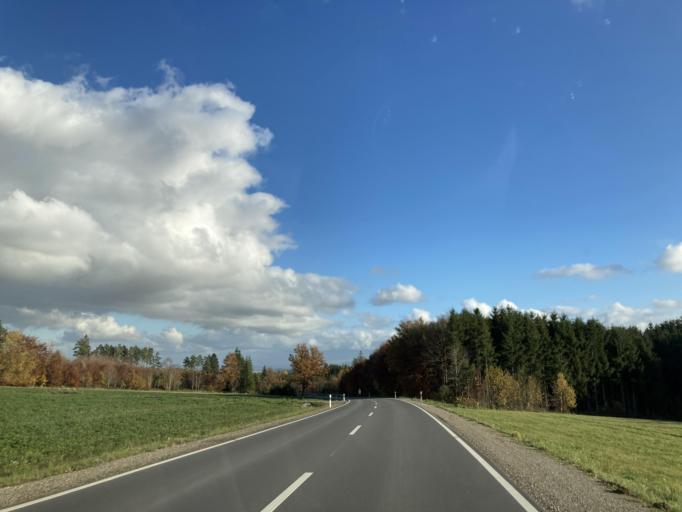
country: DE
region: Baden-Wuerttemberg
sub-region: Freiburg Region
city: Muhlheim am Bach
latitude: 48.4021
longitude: 8.6811
